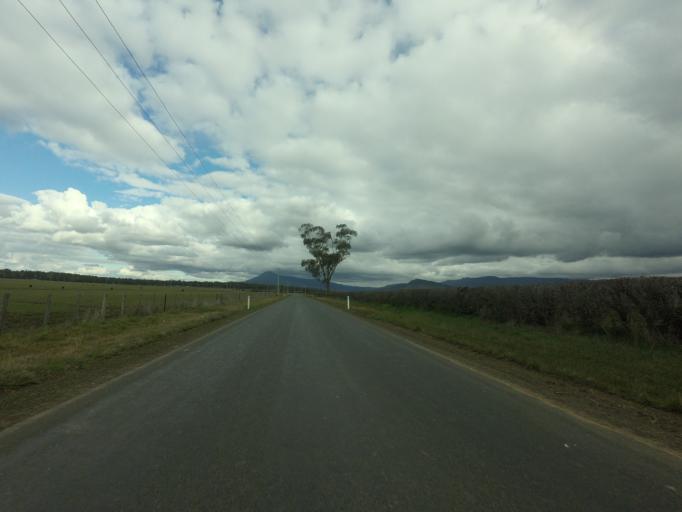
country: AU
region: Tasmania
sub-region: Northern Midlands
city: Longford
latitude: -41.7913
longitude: 147.1131
